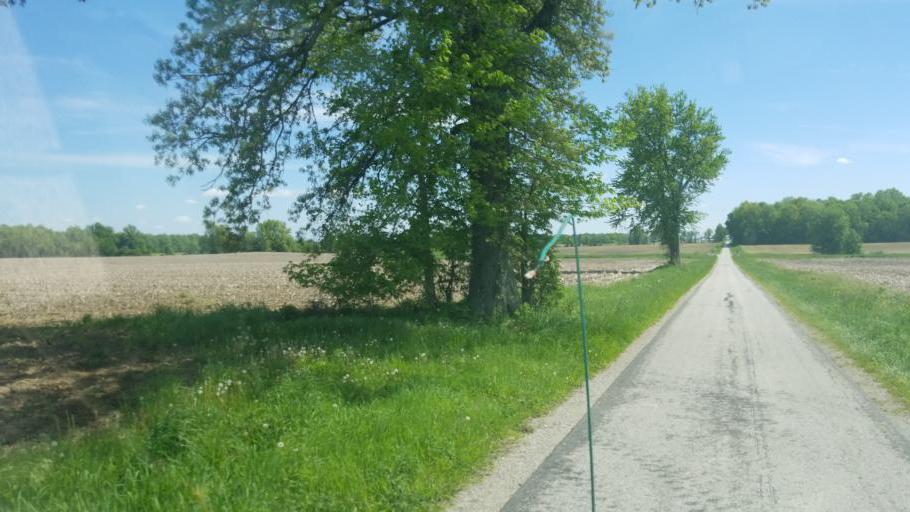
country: US
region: Ohio
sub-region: Huron County
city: Willard
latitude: 41.0484
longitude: -82.9390
